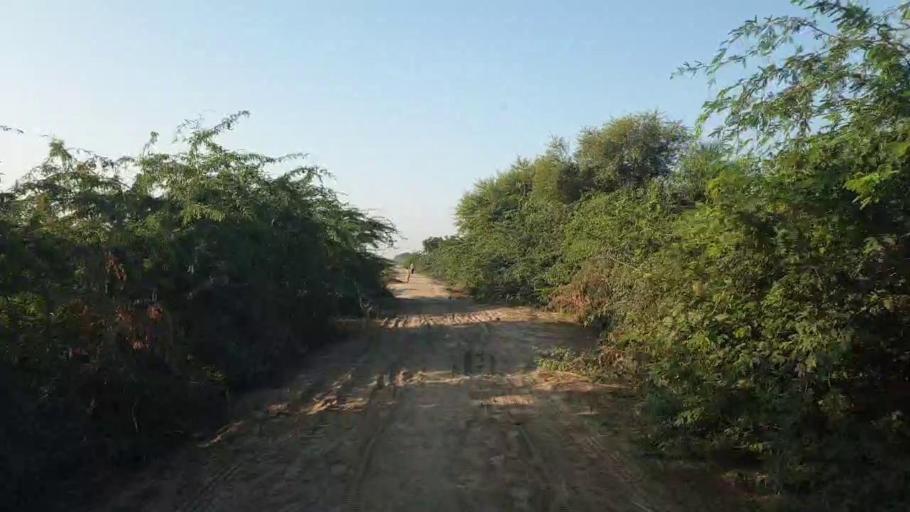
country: PK
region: Sindh
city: Badin
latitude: 24.6150
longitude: 68.7863
